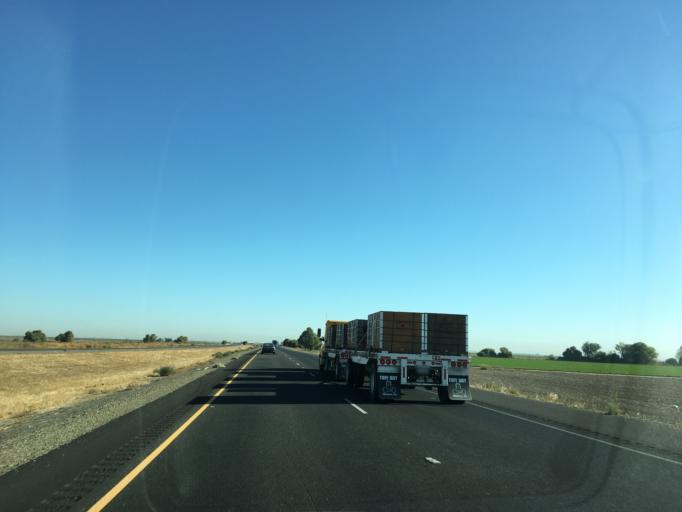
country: US
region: California
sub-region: Merced County
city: Dos Palos
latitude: 37.0577
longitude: -120.5470
